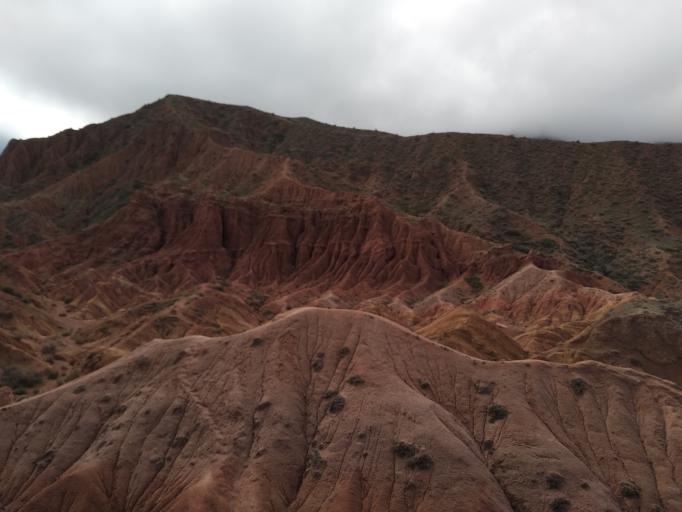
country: KG
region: Ysyk-Koel
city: Kadzhi-Say
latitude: 42.1565
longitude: 77.3552
